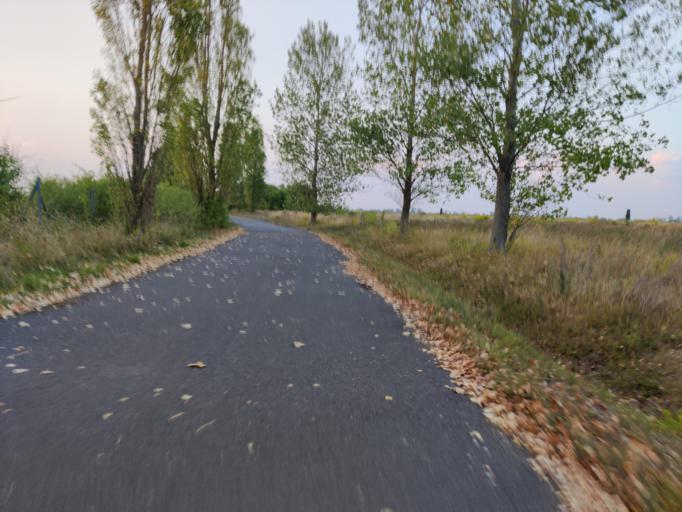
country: DE
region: Saxony
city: Zschortau
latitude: 51.4534
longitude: 12.3185
